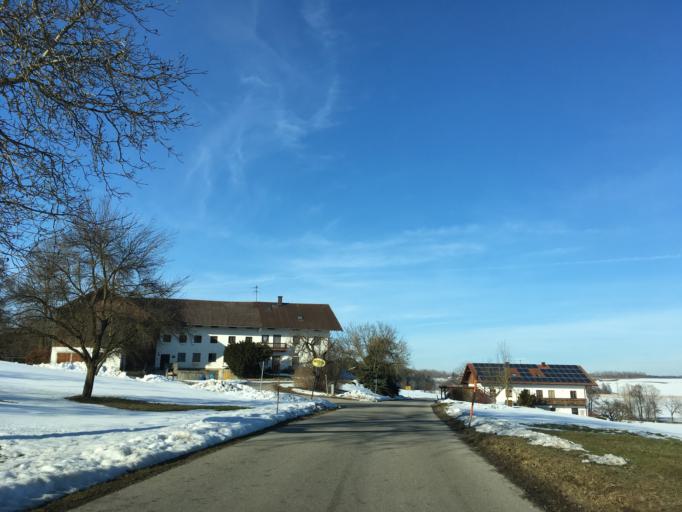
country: DE
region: Bavaria
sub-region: Upper Bavaria
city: Steinhoring
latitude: 48.0988
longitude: 12.0197
